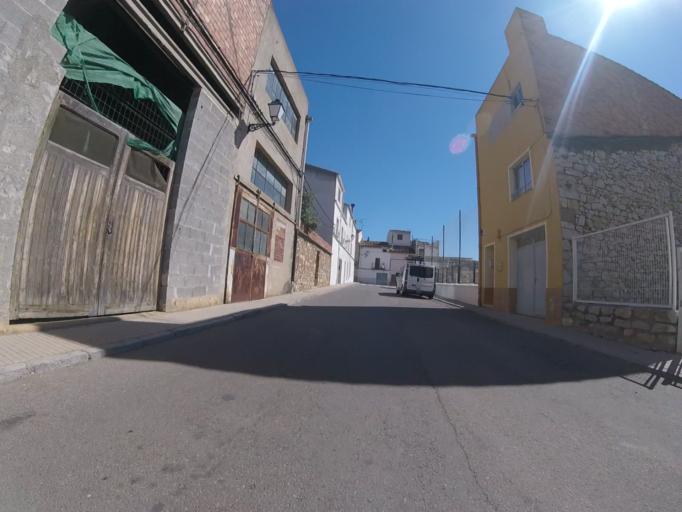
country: ES
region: Valencia
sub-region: Provincia de Castello
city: Chert/Xert
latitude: 40.4163
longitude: 0.1745
